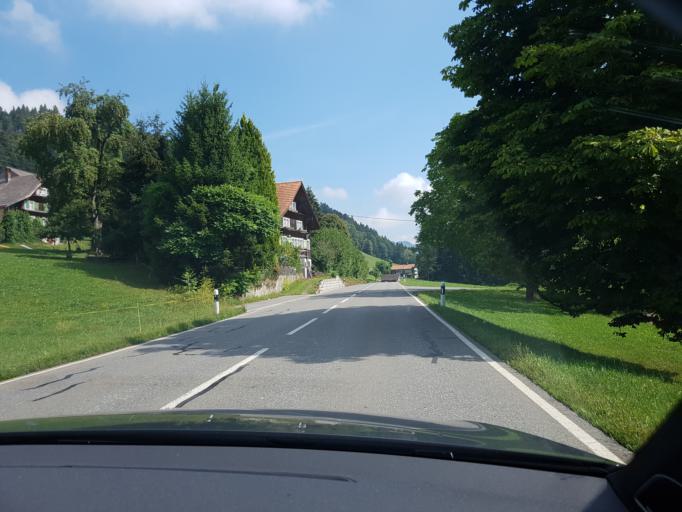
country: CH
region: Saint Gallen
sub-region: Wahlkreis Toggenburg
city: Wattwil
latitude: 47.2772
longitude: 9.0674
